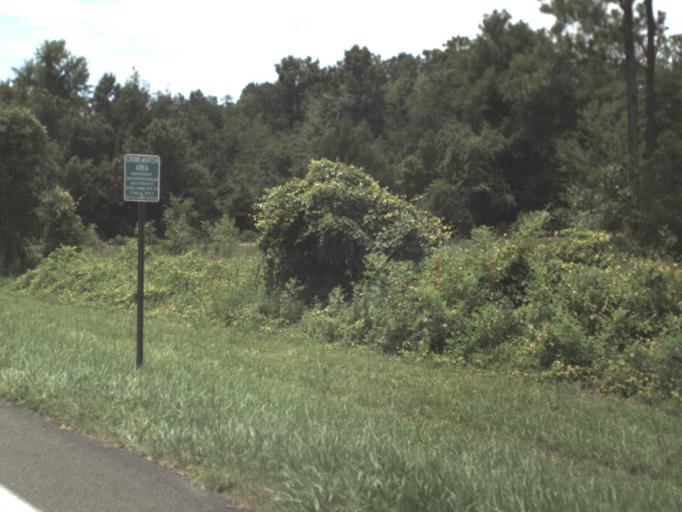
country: US
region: Florida
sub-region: Levy County
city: Williston
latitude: 29.4569
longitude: -82.4749
